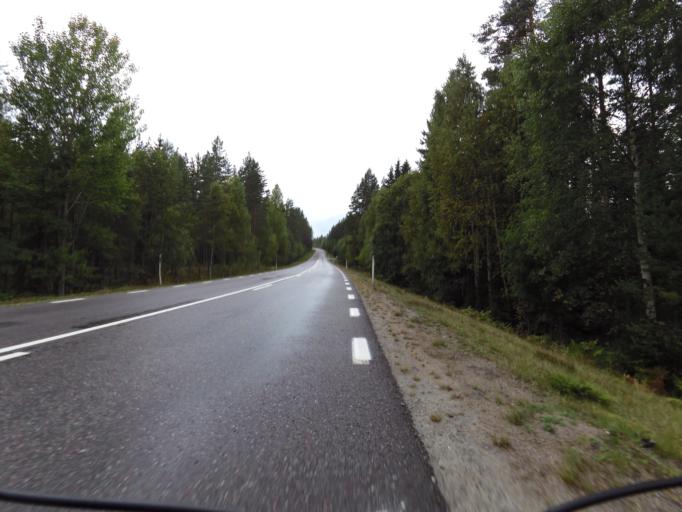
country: SE
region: Gaevleborg
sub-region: Ockelbo Kommun
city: Ockelbo
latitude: 60.8793
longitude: 16.8791
